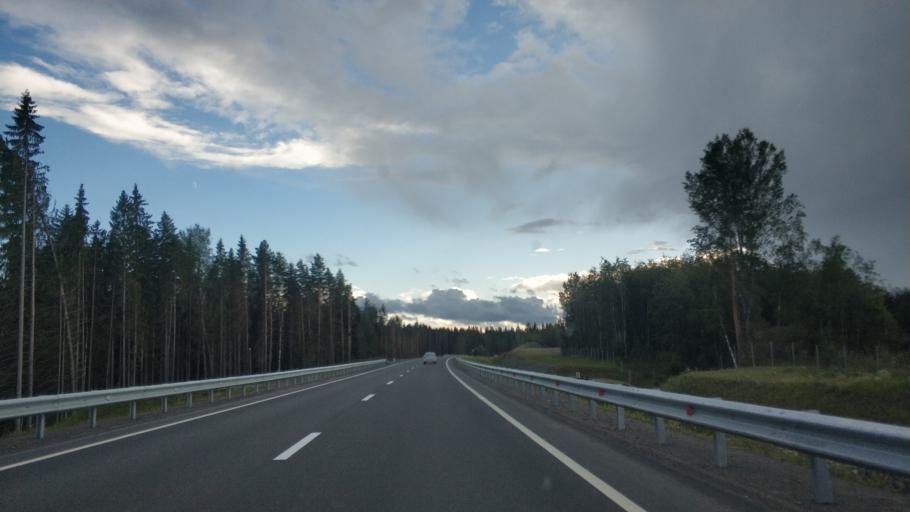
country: RU
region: Republic of Karelia
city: Lakhdenpokh'ya
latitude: 61.4783
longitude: 30.0077
